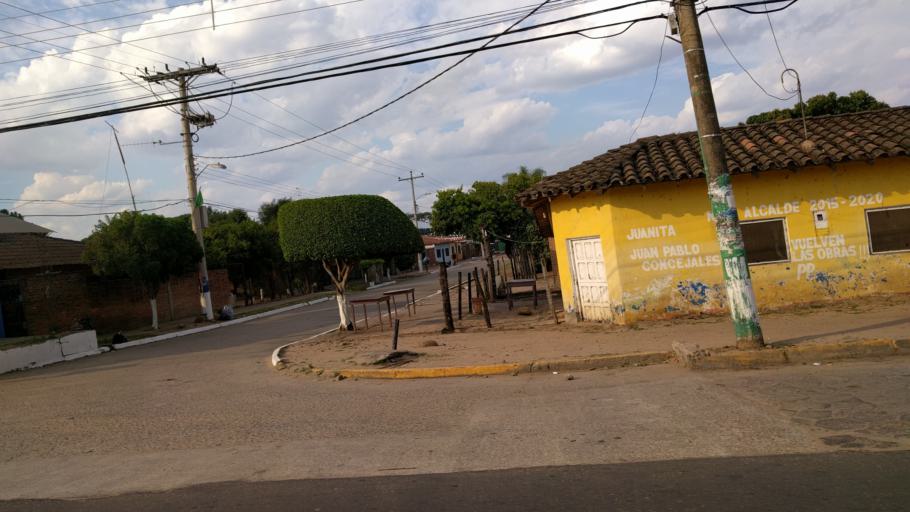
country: BO
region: Santa Cruz
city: Warnes
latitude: -17.5142
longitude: -63.1659
